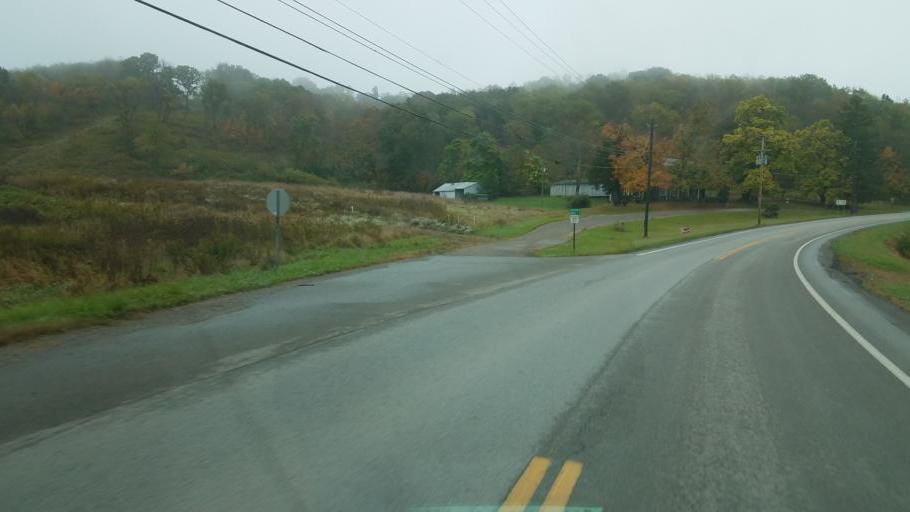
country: US
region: Ohio
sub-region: Carroll County
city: Carrollton
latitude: 40.4081
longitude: -81.1004
